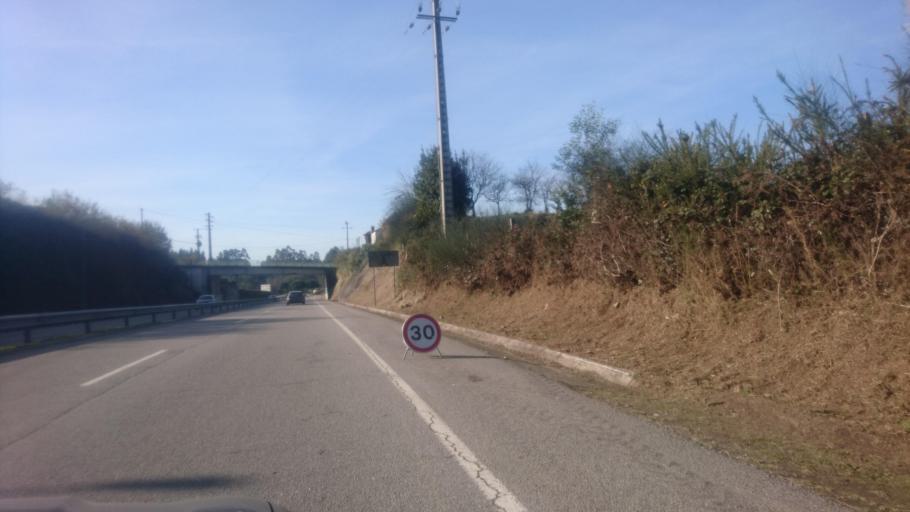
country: PT
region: Aveiro
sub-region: Santa Maria da Feira
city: Rio Meao
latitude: 40.9268
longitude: -8.5760
